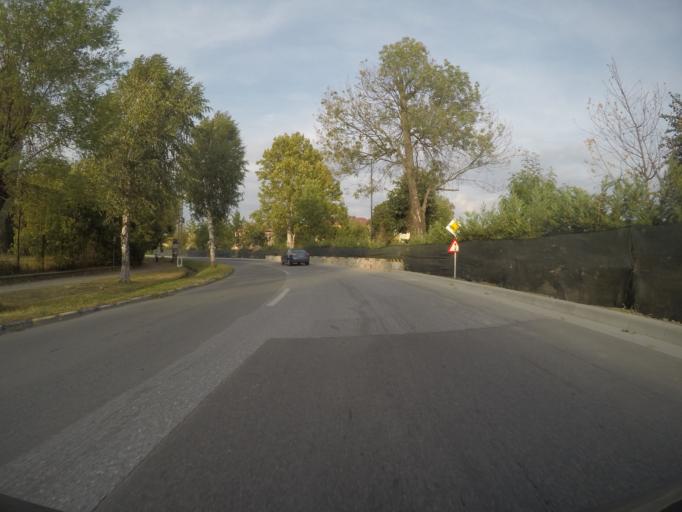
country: RO
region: Alba
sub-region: Municipiul Sebes
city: Sebes
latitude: 45.9553
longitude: 23.5728
